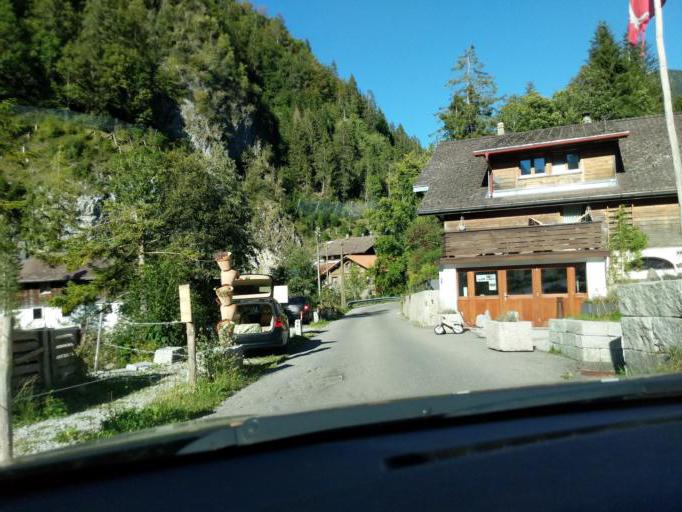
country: CH
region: Bern
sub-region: Obersimmental-Saanen District
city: Zweisimmen
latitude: 46.6098
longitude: 7.2843
